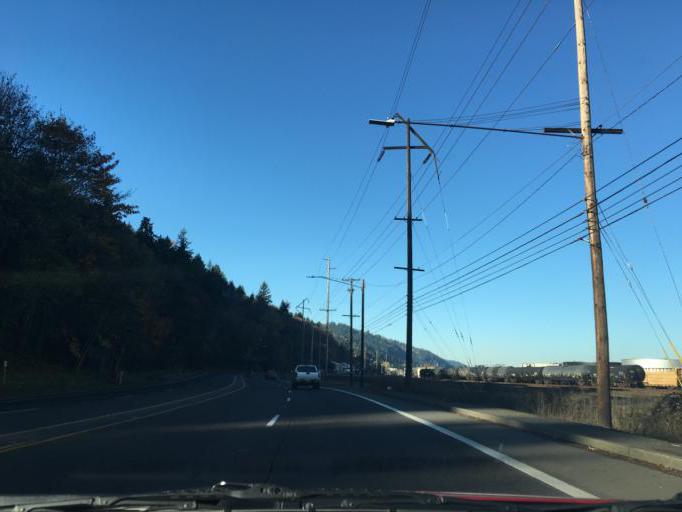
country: US
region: Oregon
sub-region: Washington County
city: West Haven
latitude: 45.5566
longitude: -122.7355
